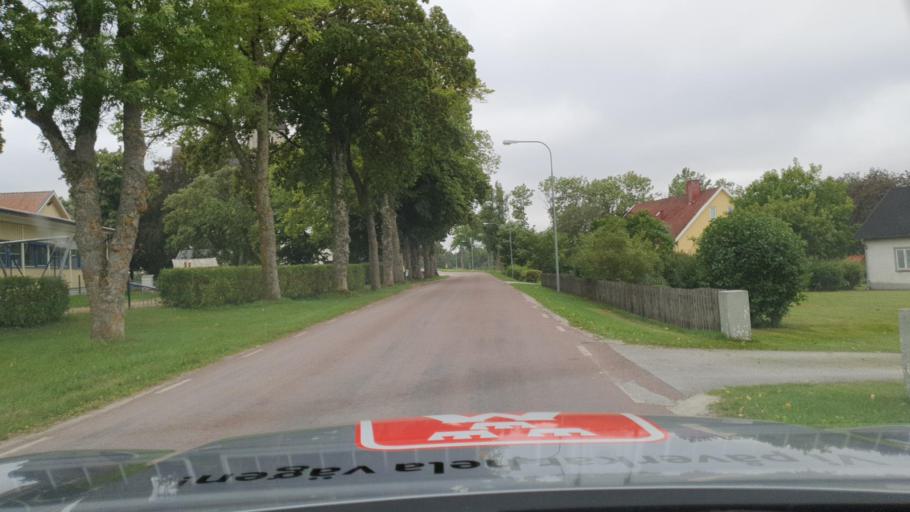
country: SE
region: Gotland
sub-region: Gotland
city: Visby
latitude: 57.6113
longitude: 18.4664
